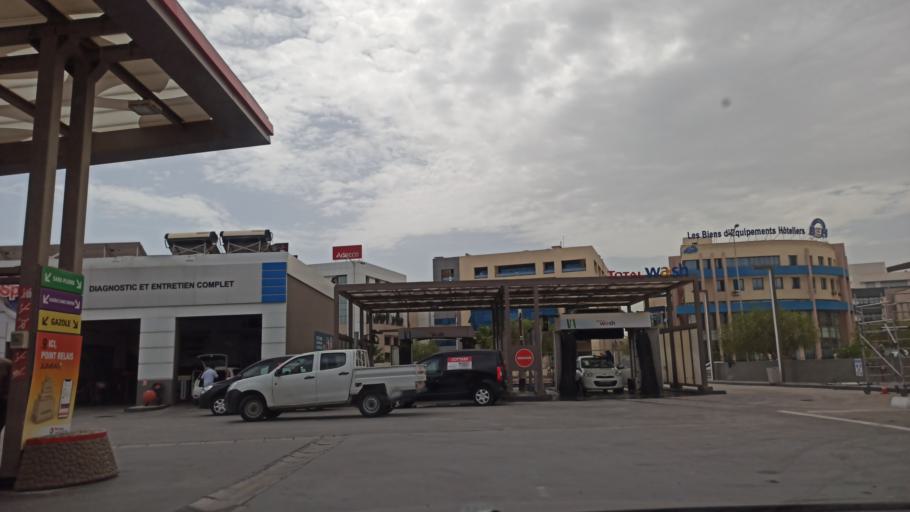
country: TN
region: Tunis
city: La Goulette
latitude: 36.8491
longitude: 10.2658
